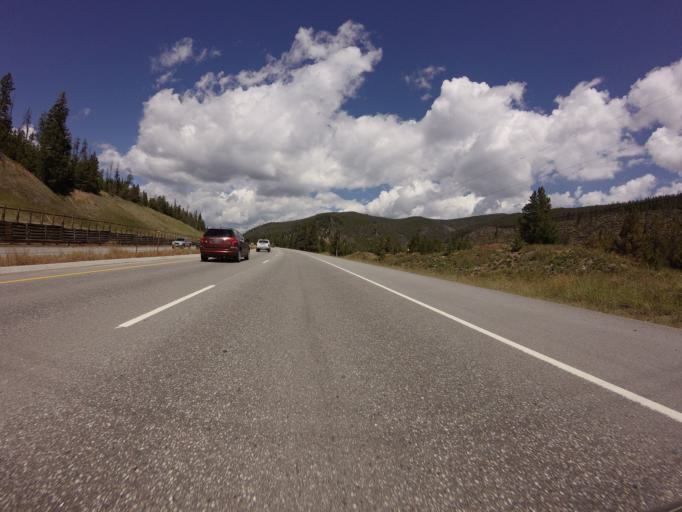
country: US
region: Colorado
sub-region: Summit County
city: Frisco
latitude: 39.5480
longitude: -106.0404
